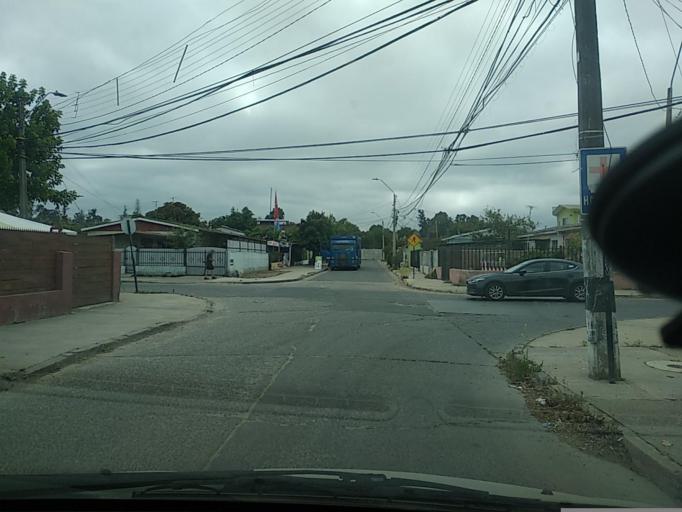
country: CL
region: Valparaiso
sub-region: Provincia de Marga Marga
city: Villa Alemana
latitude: -33.0401
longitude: -71.3621
